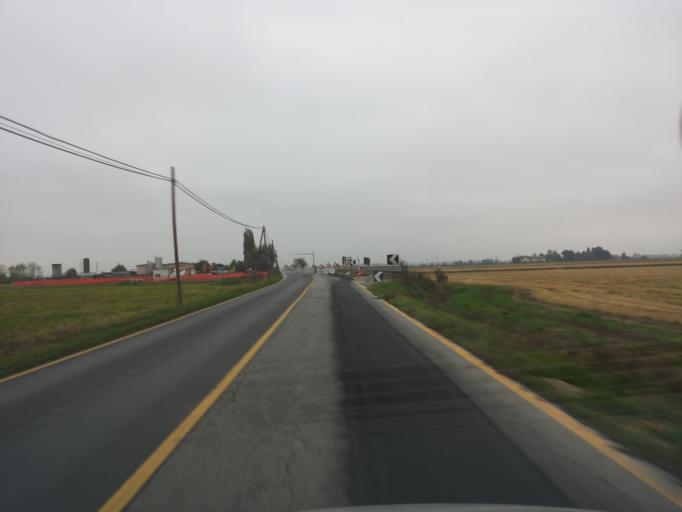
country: IT
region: Piedmont
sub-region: Provincia di Novara
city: Lumellogno
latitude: 45.4045
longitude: 8.5517
